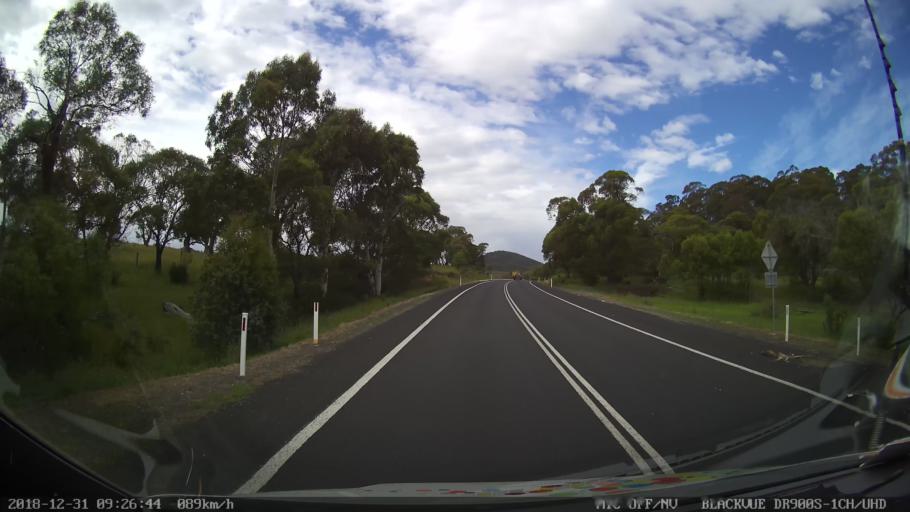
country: AU
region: New South Wales
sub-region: Snowy River
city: Jindabyne
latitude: -36.4516
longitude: 148.4936
